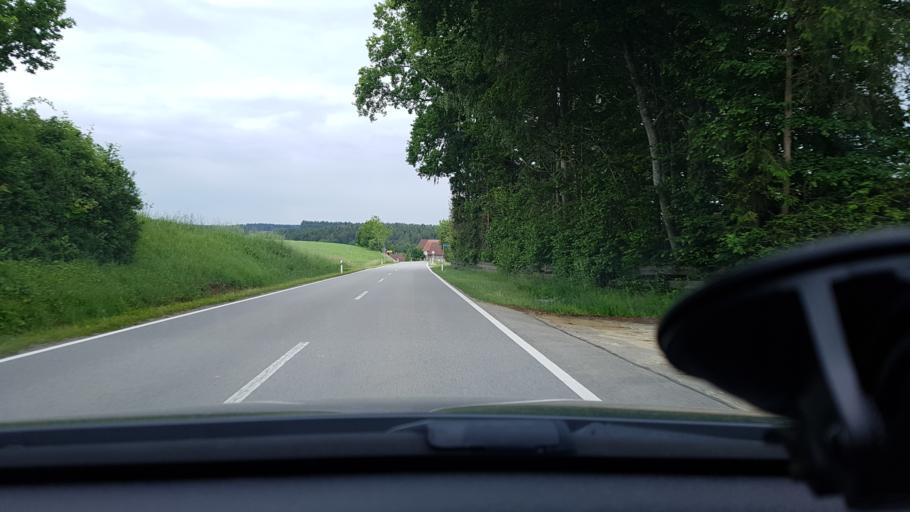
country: DE
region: Bavaria
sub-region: Lower Bavaria
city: Triftern
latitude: 48.3629
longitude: 13.0072
